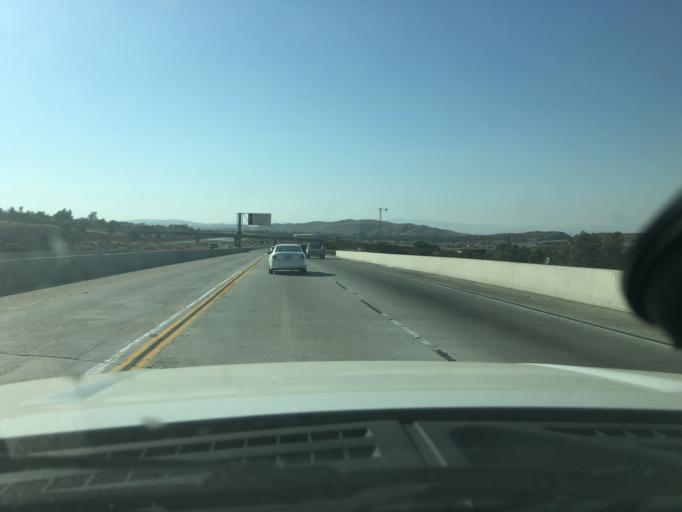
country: US
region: California
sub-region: Los Angeles County
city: Palmdale
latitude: 34.5439
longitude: -118.1267
